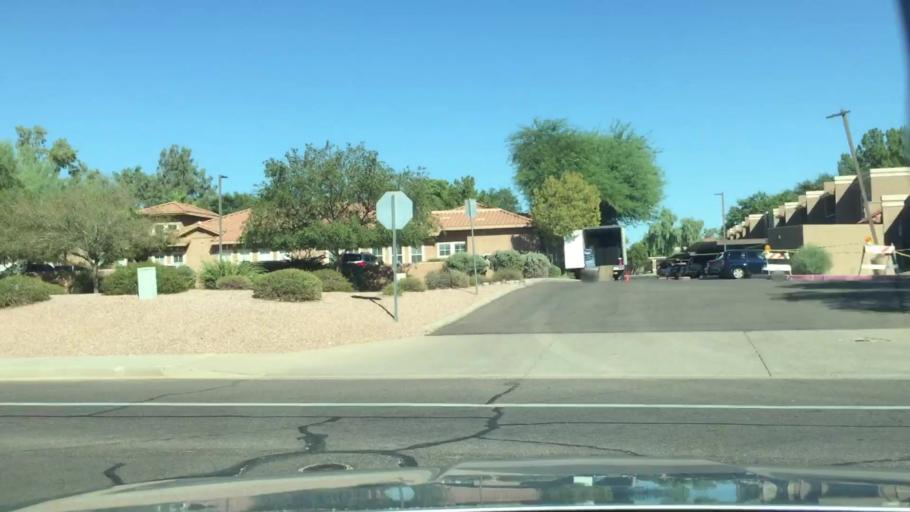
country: US
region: Arizona
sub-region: Maricopa County
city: Gilbert
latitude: 33.4065
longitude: -111.6762
